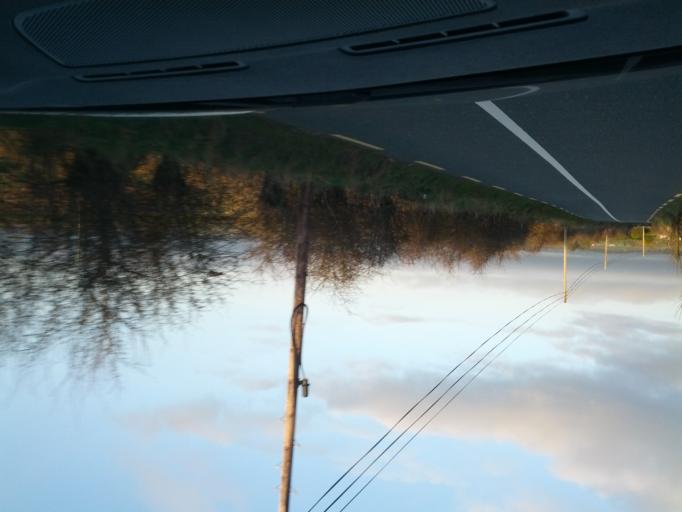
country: IE
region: Connaught
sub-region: Sligo
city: Tobercurry
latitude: 54.0446
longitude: -8.6731
